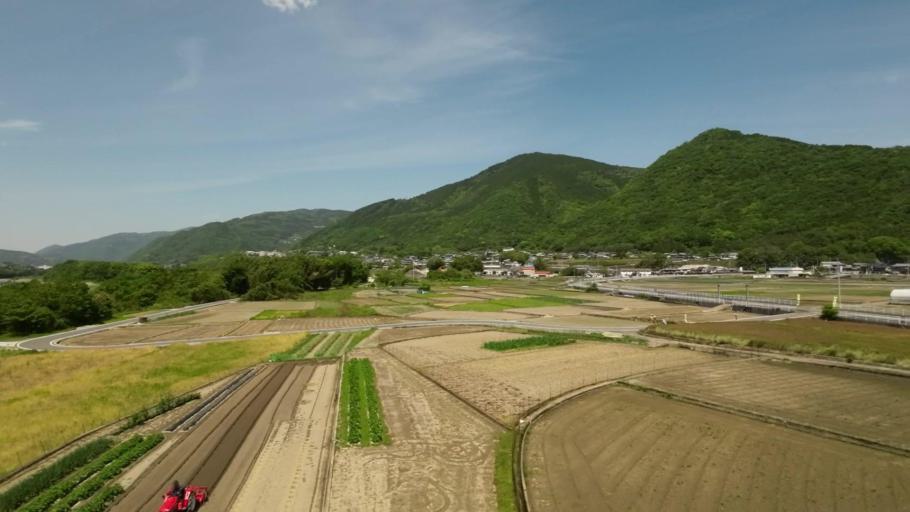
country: JP
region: Tokushima
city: Ikedacho
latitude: 34.0374
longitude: 133.8648
